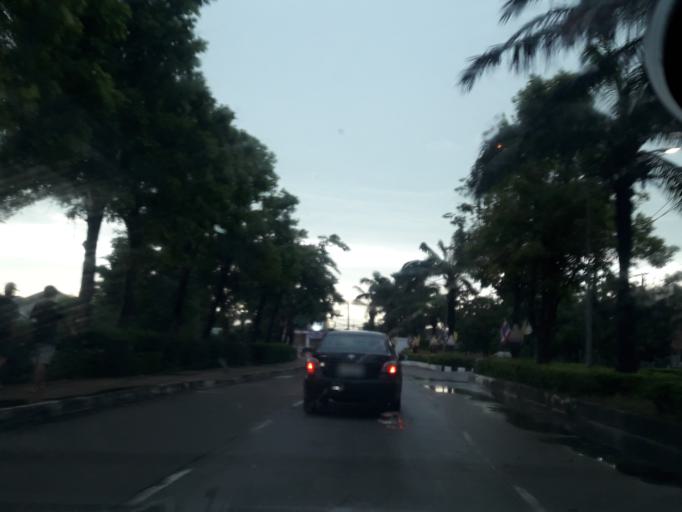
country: TH
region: Pathum Thani
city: Lam Luk Ka
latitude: 13.9372
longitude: 100.7399
